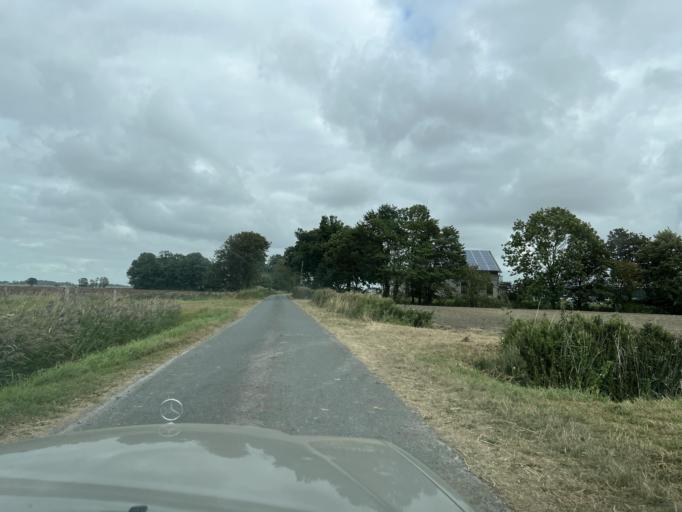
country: DE
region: Schleswig-Holstein
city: Groven
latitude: 54.3000
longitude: 8.9907
